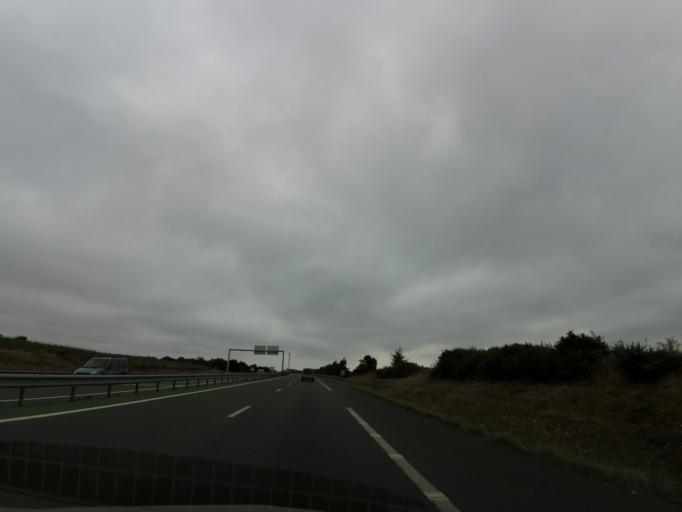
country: FR
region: Pays de la Loire
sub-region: Departement de la Vendee
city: La Ferriere
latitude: 46.6749
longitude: -1.3405
